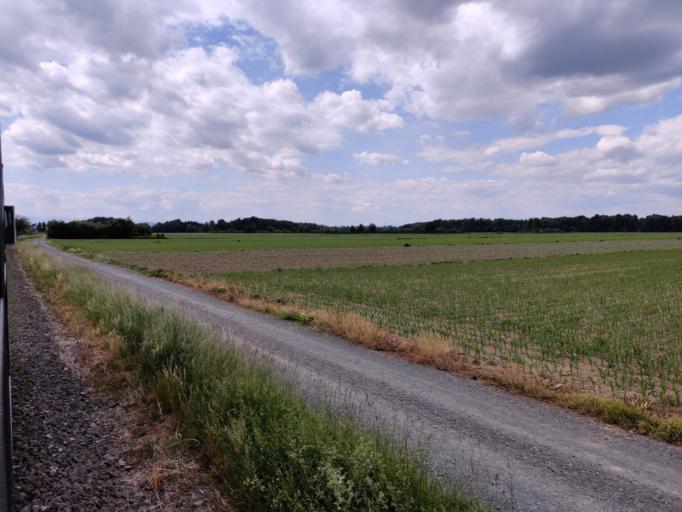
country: SI
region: Sentilj
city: Selnica ob Muri
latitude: 46.7147
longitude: 15.6918
